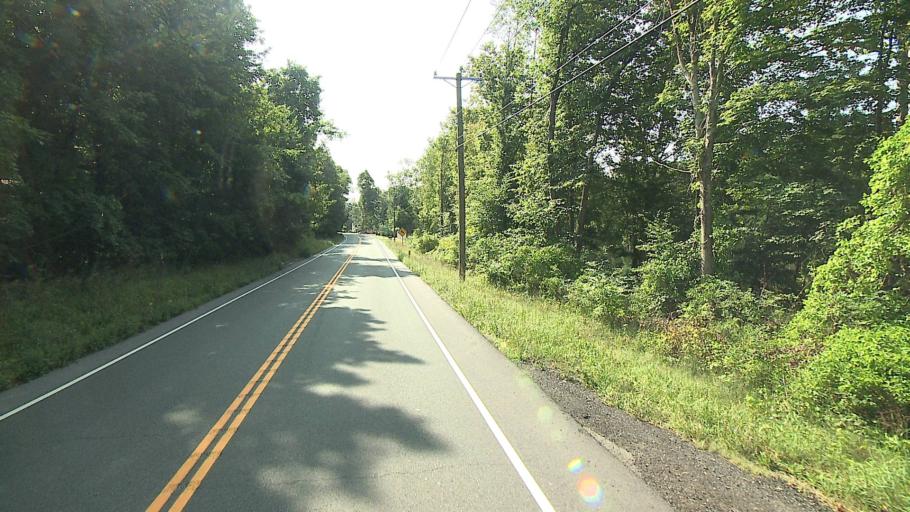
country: US
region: Connecticut
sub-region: Fairfield County
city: Sherman
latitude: 41.6515
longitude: -73.4879
